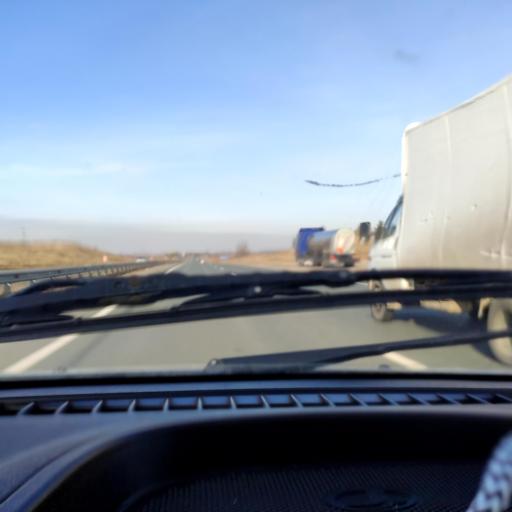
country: RU
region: Samara
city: Zhigulevsk
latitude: 53.5062
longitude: 49.5385
